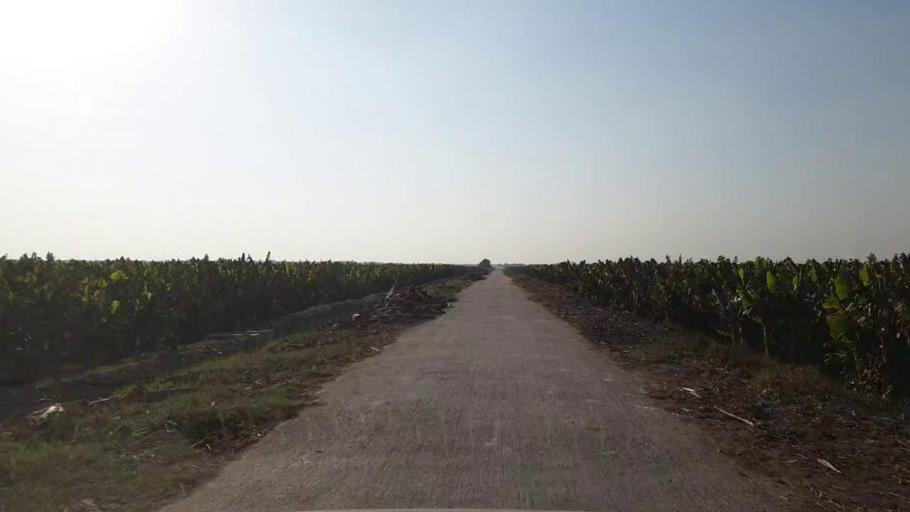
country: PK
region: Sindh
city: Tando Allahyar
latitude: 25.3467
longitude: 68.6786
